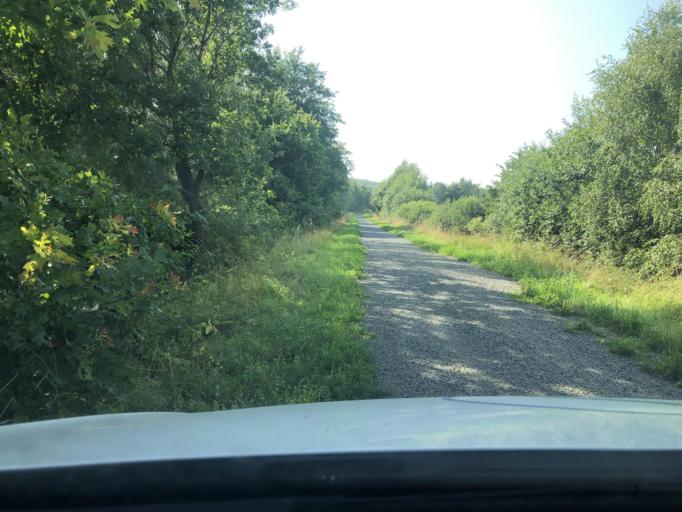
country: SE
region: Skane
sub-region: Kristianstads Kommun
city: Degeberga
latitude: 55.8251
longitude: 14.1008
